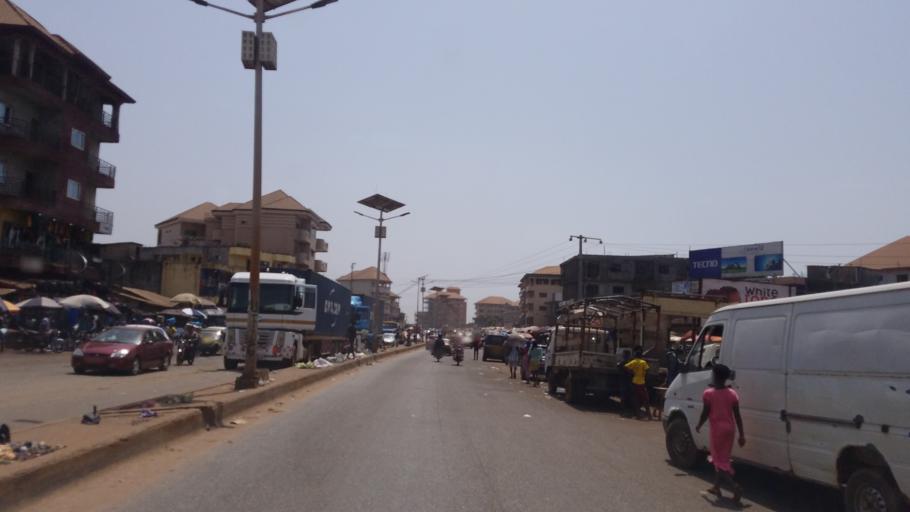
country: GN
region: Kindia
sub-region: Prefecture de Dubreka
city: Dubreka
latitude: 9.6670
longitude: -13.5600
